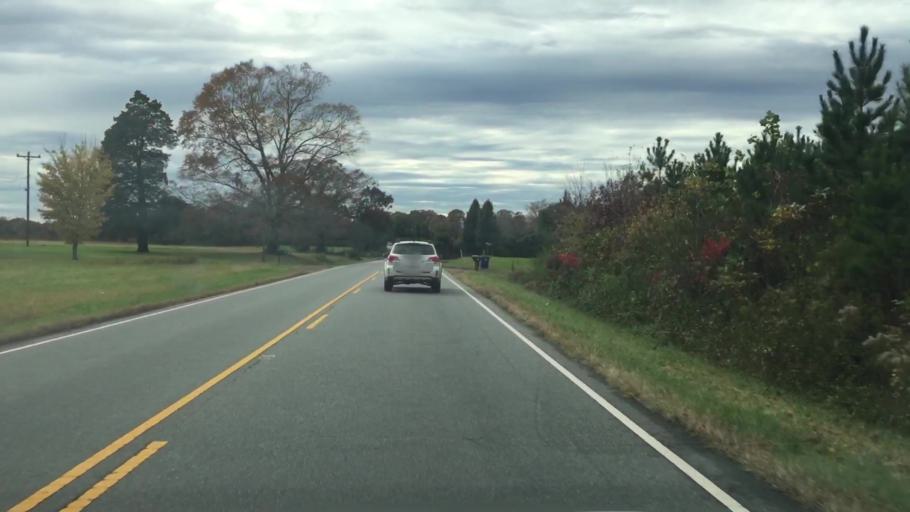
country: US
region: North Carolina
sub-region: Guilford County
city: Summerfield
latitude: 36.2759
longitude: -79.7990
